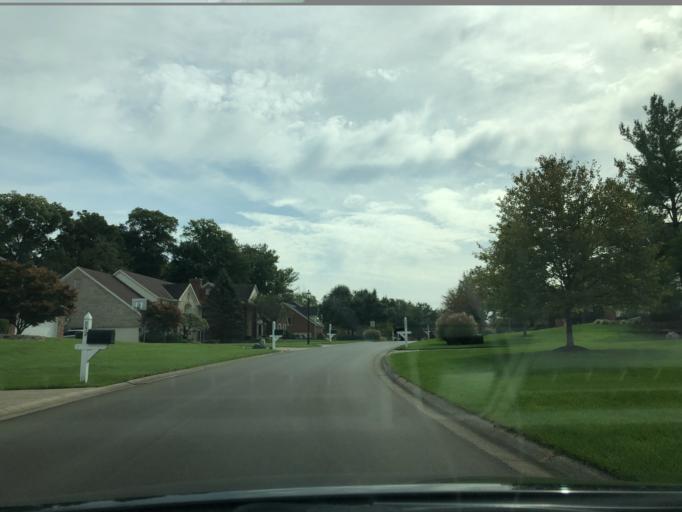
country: US
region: Ohio
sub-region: Hamilton County
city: Loveland
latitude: 39.2471
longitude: -84.2649
